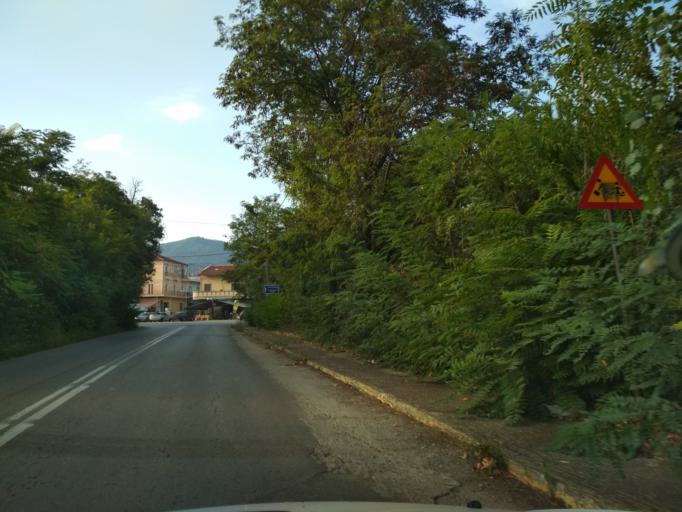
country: GR
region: Central Greece
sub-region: Nomos Evvoias
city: Prokopion
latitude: 38.7356
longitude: 23.4926
